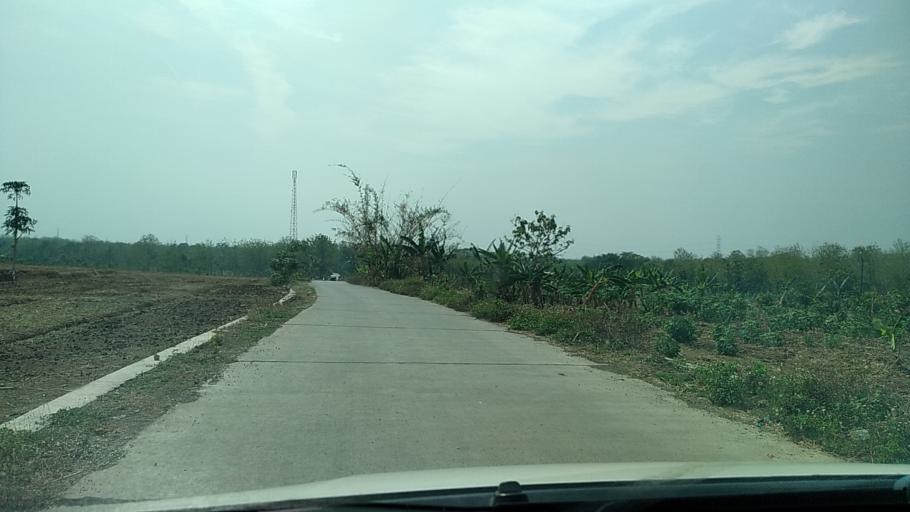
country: ID
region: Central Java
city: Mranggen
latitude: -7.0657
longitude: 110.4938
